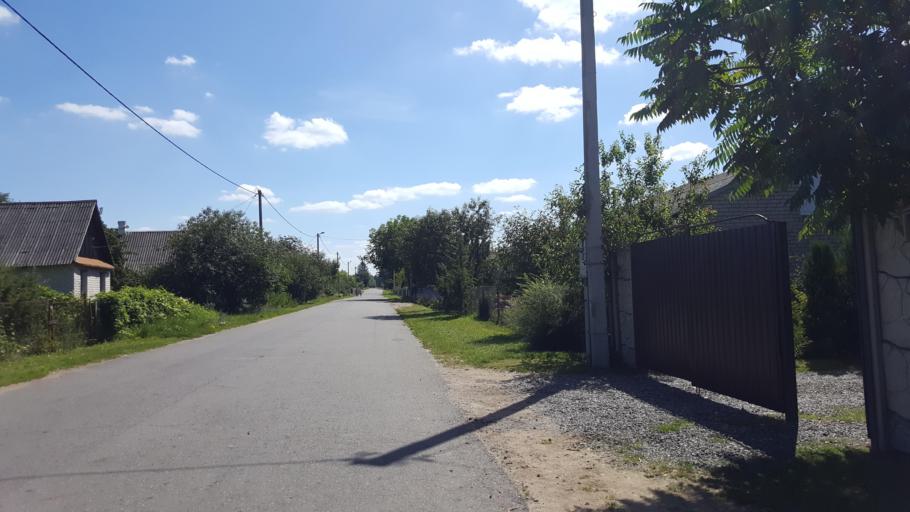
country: BY
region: Brest
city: Charnawchytsy
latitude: 52.3434
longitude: 23.6196
